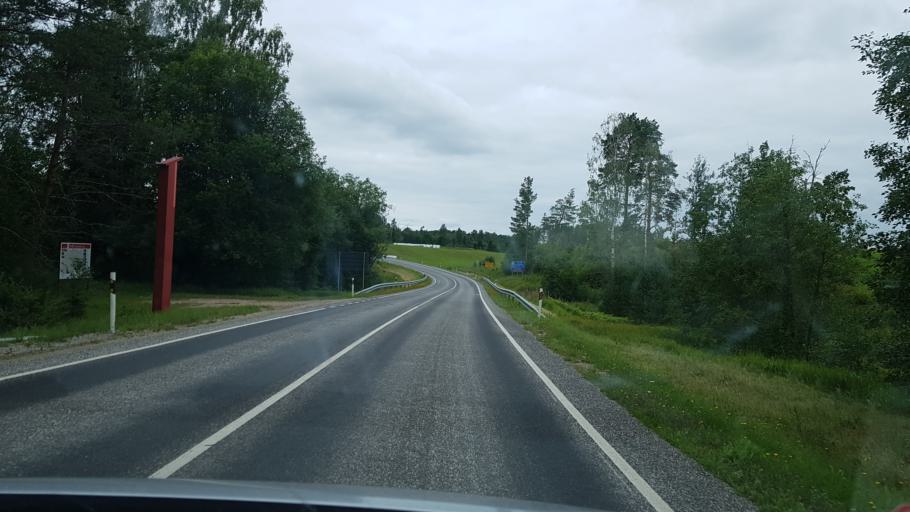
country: EE
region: Vorumaa
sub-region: Antsla vald
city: Vana-Antsla
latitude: 58.0190
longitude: 26.5867
